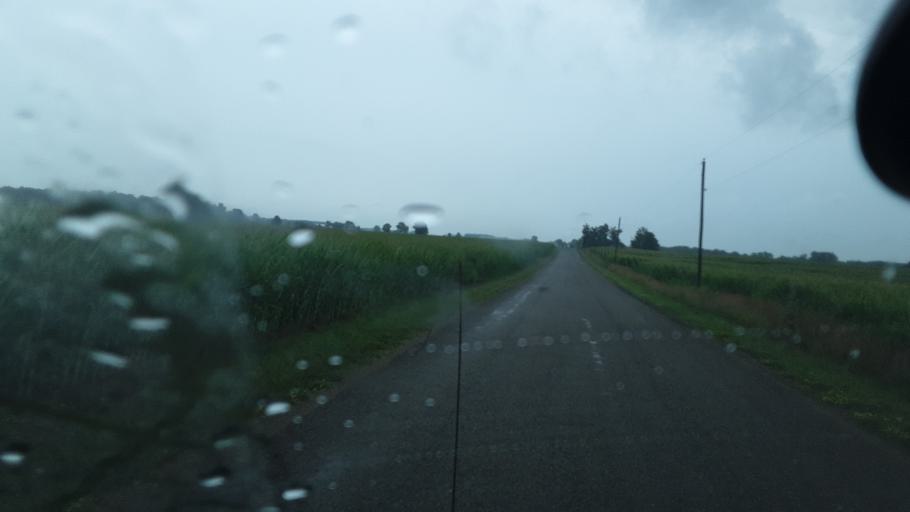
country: US
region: Indiana
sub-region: Steuben County
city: Hamilton
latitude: 41.5372
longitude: -84.8159
